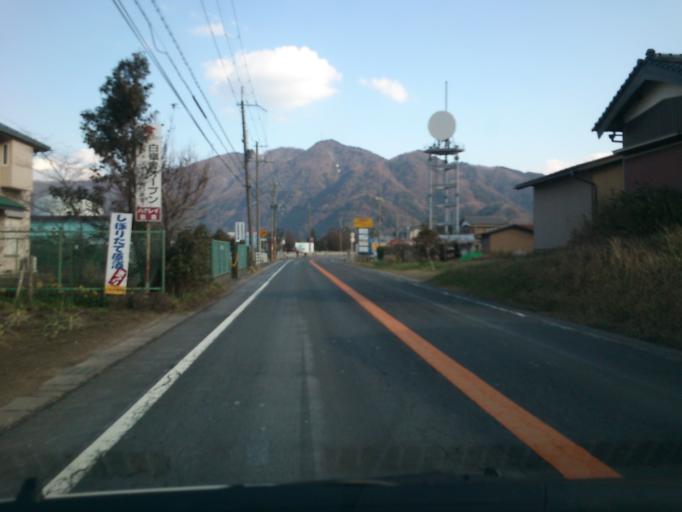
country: JP
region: Kyoto
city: Maizuru
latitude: 35.5184
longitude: 135.2828
